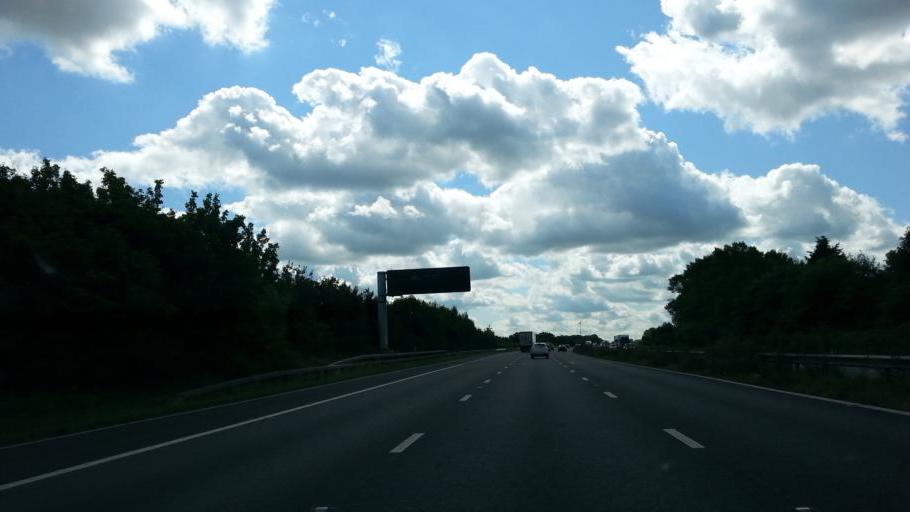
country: GB
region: England
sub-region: Leicestershire
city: Cosby
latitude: 52.5625
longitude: -1.1874
